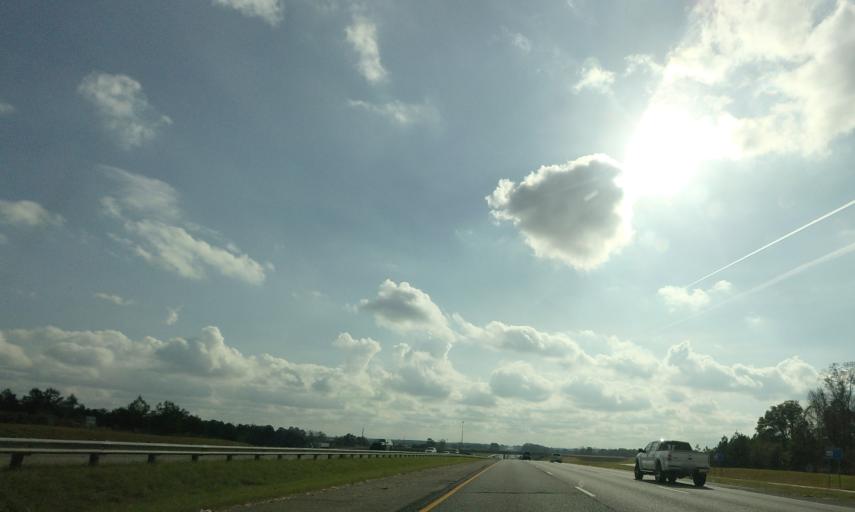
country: US
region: Georgia
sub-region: Houston County
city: Perry
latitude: 32.5508
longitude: -83.7441
